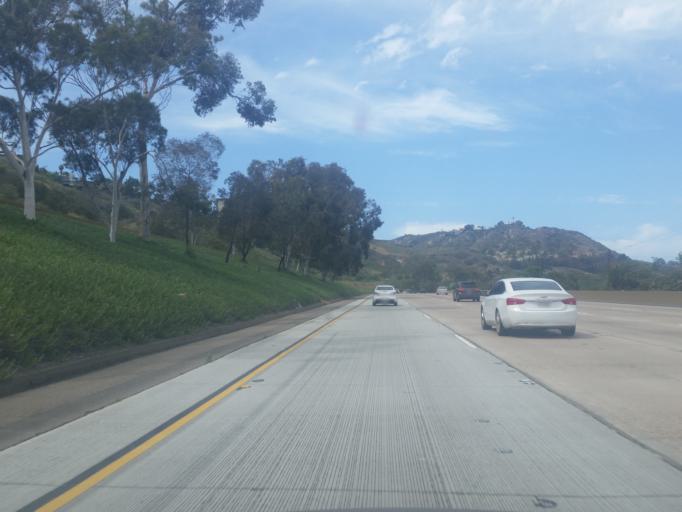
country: US
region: California
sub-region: San Diego County
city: La Jolla
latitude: 32.8217
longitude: -117.2286
